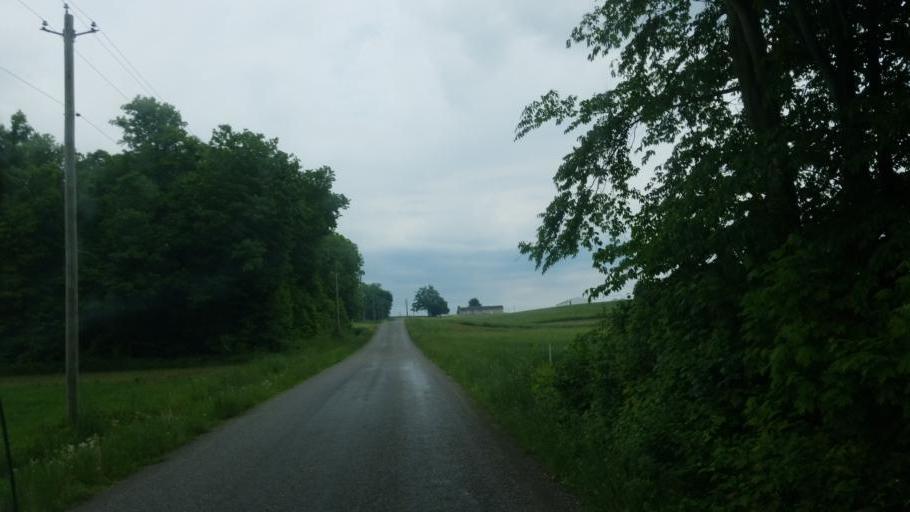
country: US
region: Ohio
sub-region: Wayne County
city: Dalton
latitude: 40.7410
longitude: -81.7121
